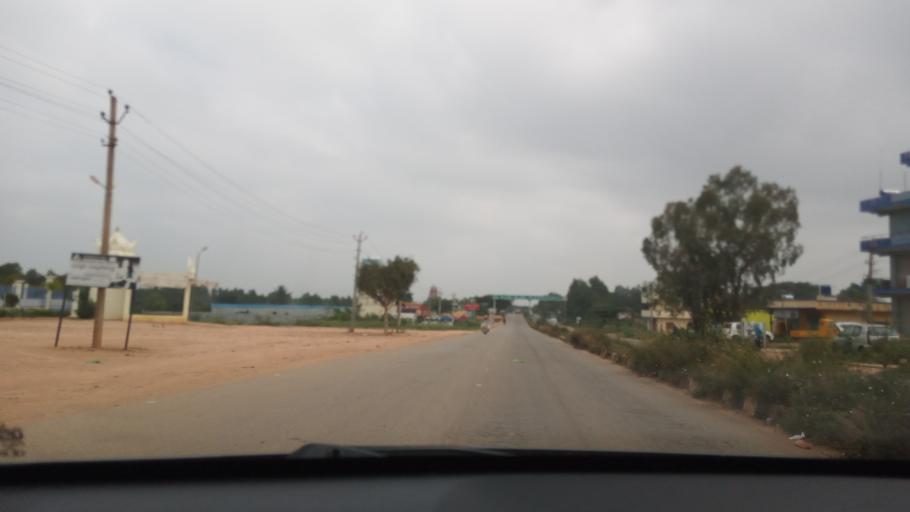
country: IN
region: Karnataka
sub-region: Bangalore Rural
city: Vijayapura
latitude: 13.2464
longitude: 77.9332
